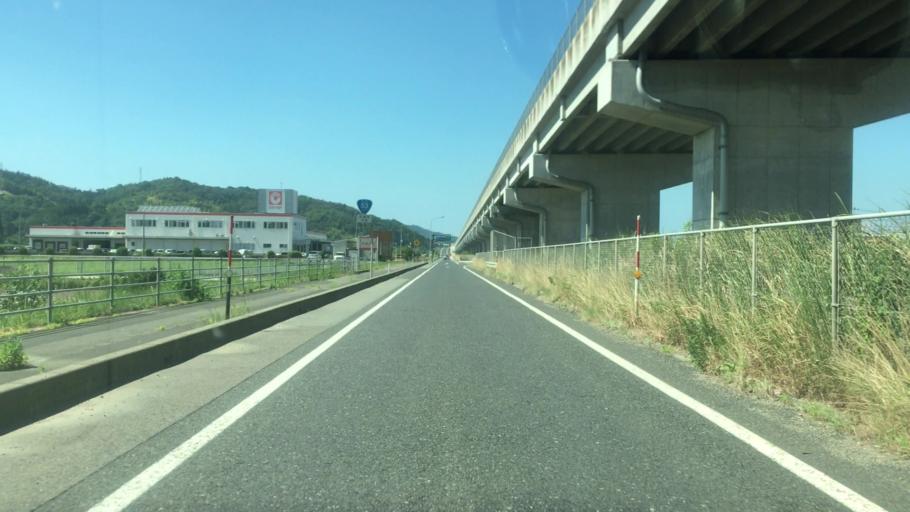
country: JP
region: Tottori
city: Tottori
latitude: 35.4268
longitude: 134.2069
